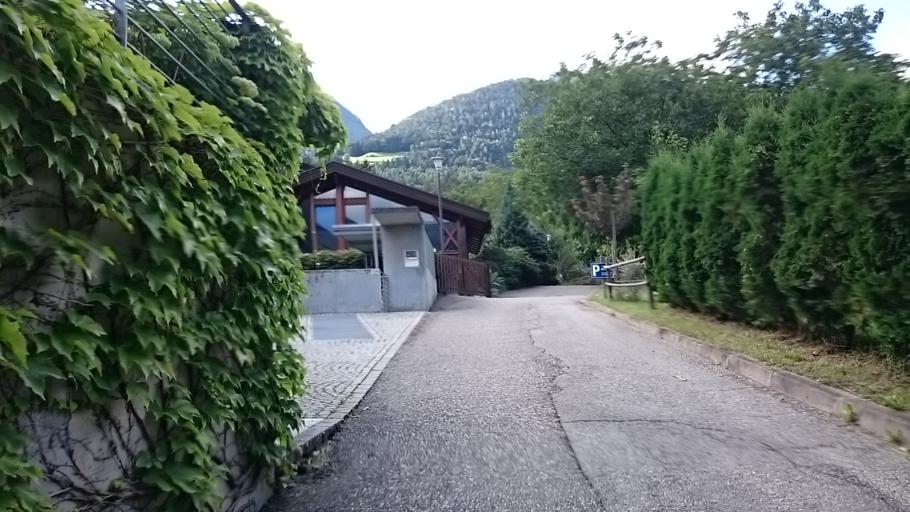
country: IT
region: Trentino-Alto Adige
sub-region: Bolzano
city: Varna
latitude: 46.7433
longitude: 11.6347
